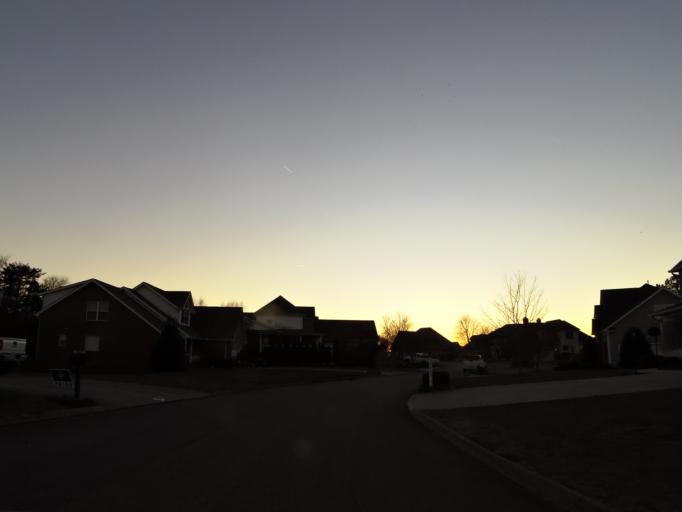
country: US
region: Tennessee
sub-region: Blount County
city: Eagleton Village
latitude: 35.8764
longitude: -83.9428
